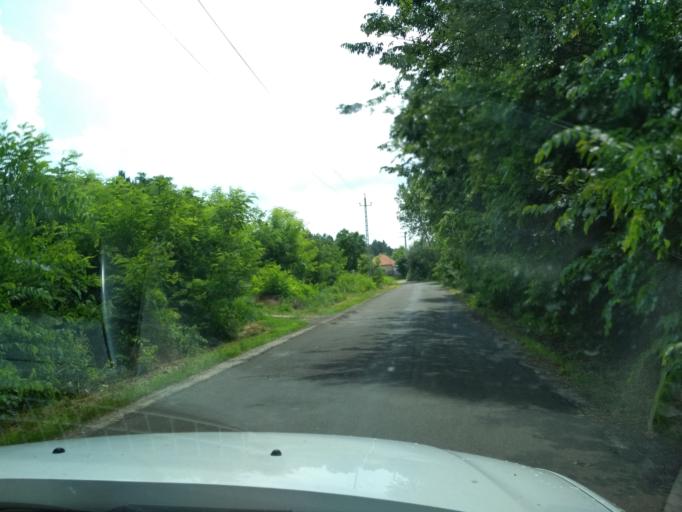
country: HU
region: Pest
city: Nagykata
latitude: 47.3843
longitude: 19.7555
